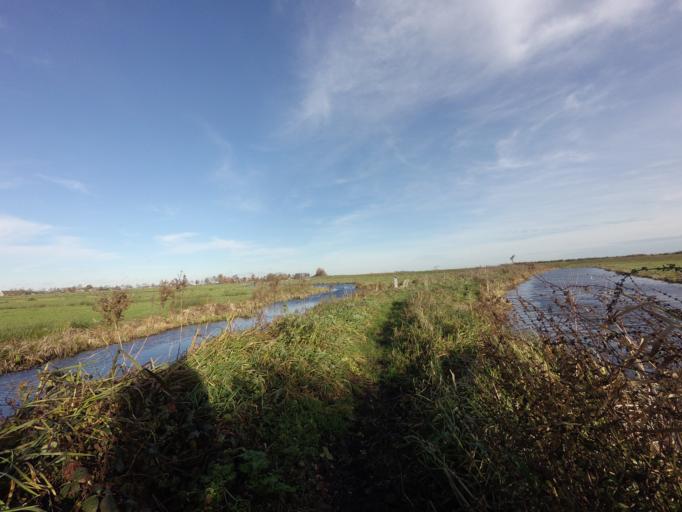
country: NL
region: South Holland
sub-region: Gemeente Vlist
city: Haastrecht
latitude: 52.0452
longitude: 4.7768
